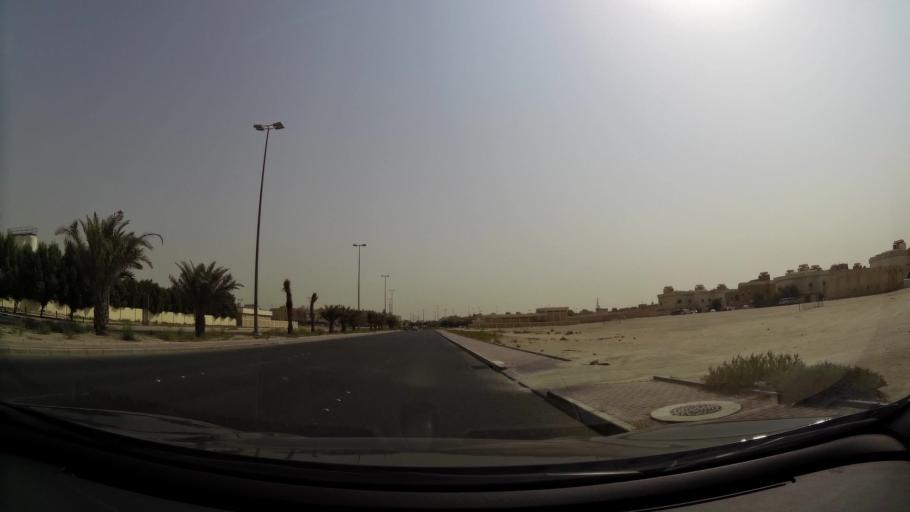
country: KW
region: Muhafazat al Jahra'
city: Al Jahra'
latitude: 29.3235
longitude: 47.7291
